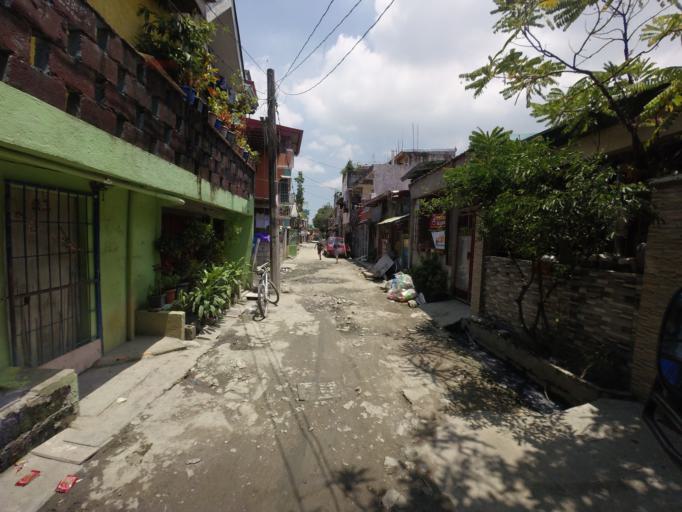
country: PH
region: Calabarzon
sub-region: Province of Rizal
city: Taytay
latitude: 14.5416
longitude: 121.1080
